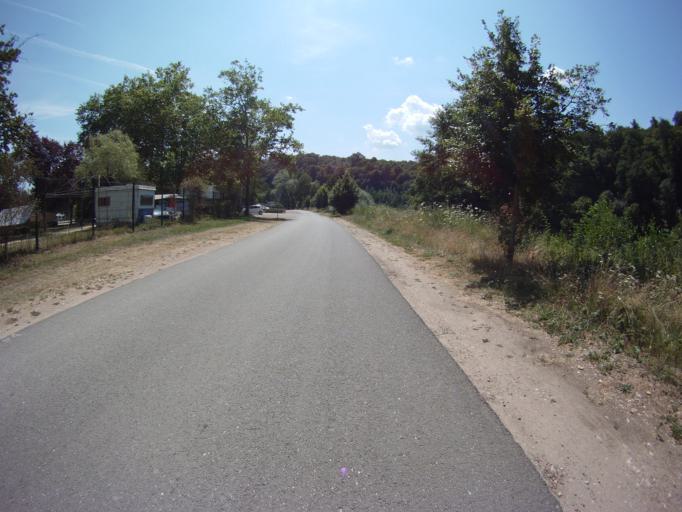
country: FR
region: Lorraine
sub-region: Departement de Meurthe-et-Moselle
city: Liverdun
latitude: 48.7478
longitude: 6.0565
